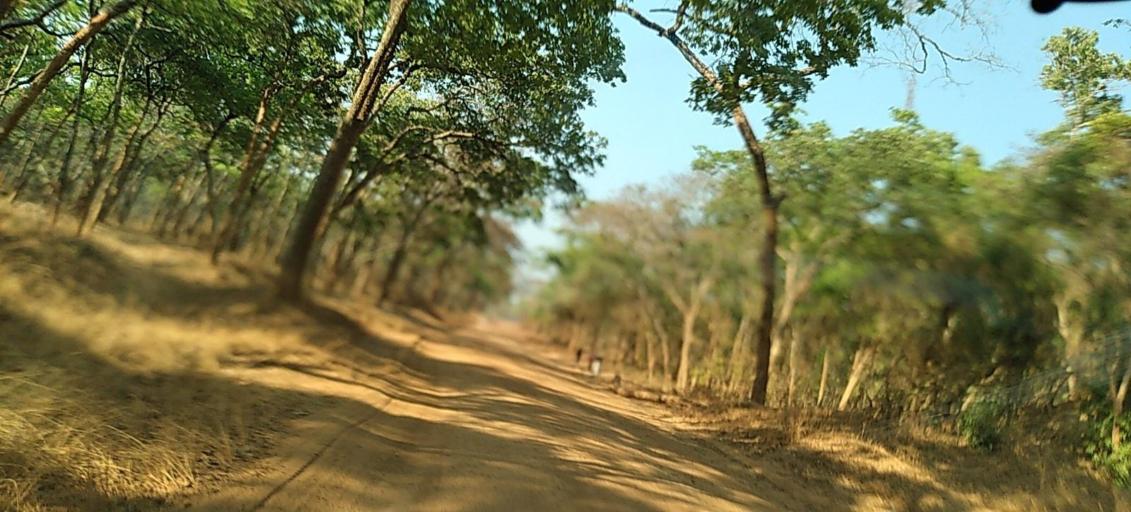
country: ZM
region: North-Western
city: Kasempa
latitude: -13.5862
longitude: 25.9864
